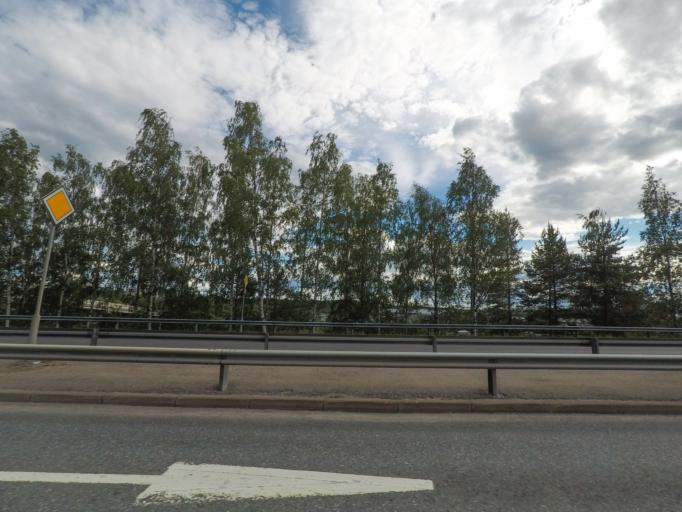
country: FI
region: Paijanne Tavastia
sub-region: Lahti
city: Lahti
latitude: 60.9771
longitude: 25.6739
